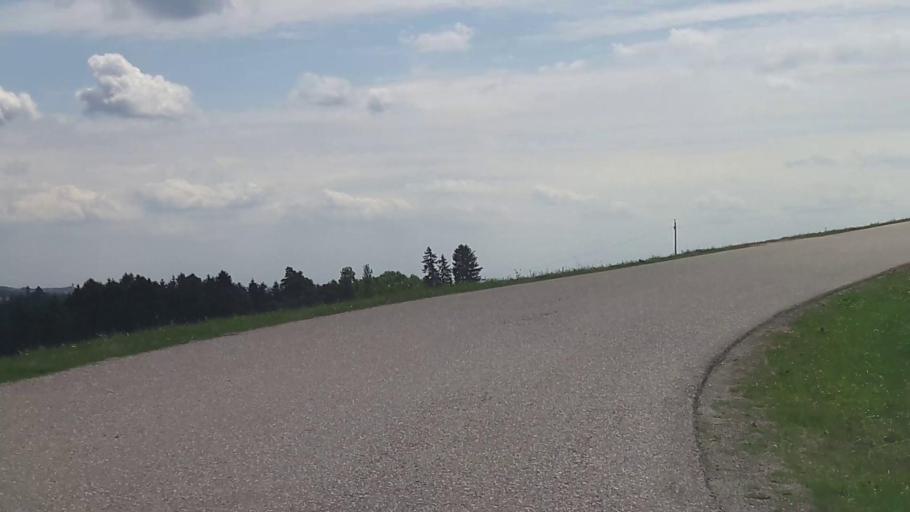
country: AT
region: Upper Austria
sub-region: Politischer Bezirk Rohrbach
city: Kleinzell im Muehlkreis
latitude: 48.4725
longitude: 13.9593
